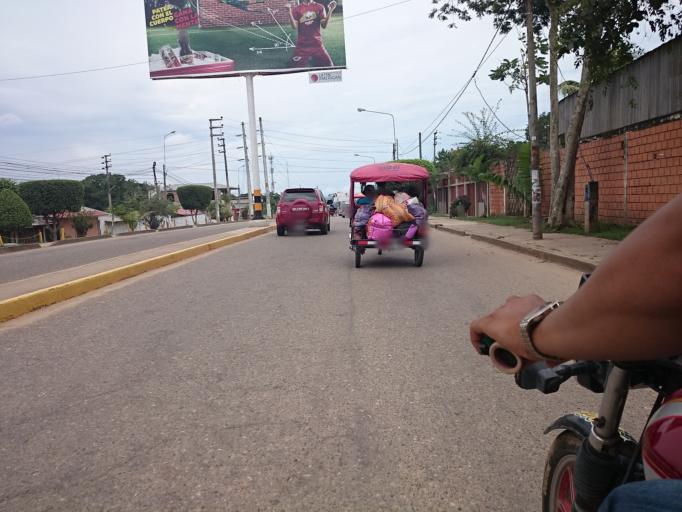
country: PE
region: Ucayali
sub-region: Provincia de Coronel Portillo
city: Puerto Callao
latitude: -8.3638
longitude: -74.5669
